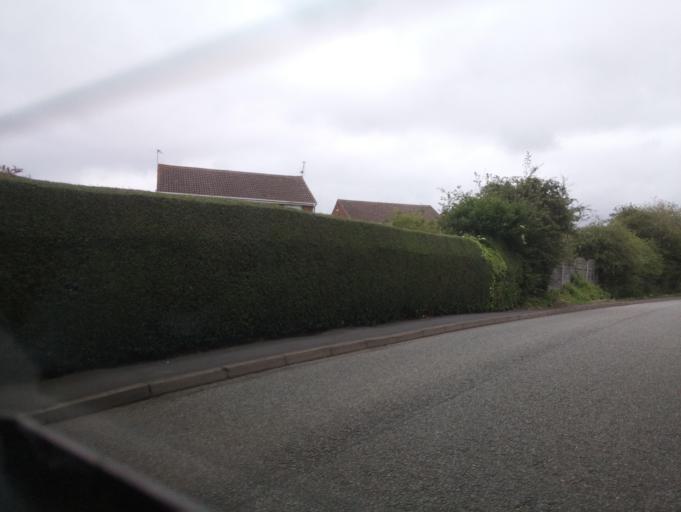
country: GB
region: England
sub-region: Leicestershire
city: Melton Mowbray
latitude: 52.7499
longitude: -0.8929
